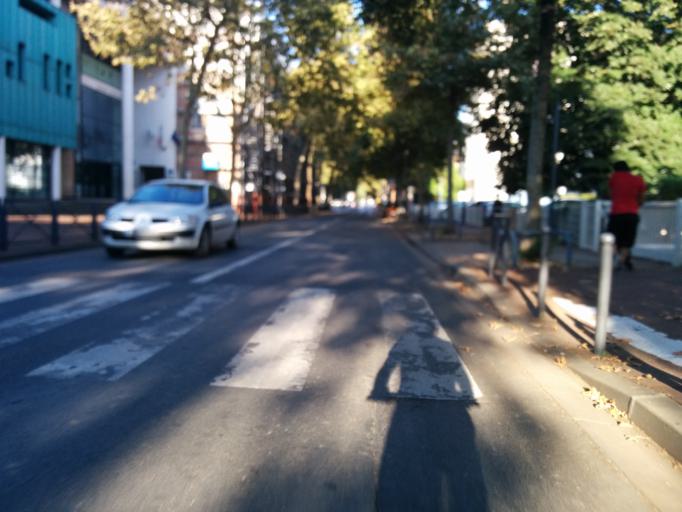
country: FR
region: Ile-de-France
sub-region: Departement des Hauts-de-Seine
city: Boulogne-Billancourt
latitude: 48.8211
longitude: 2.2577
